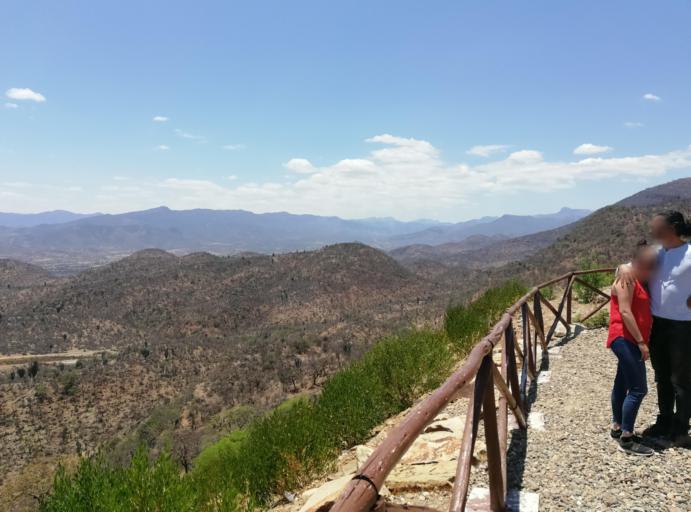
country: BO
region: Cochabamba
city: Aiquile
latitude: -18.1314
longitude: -64.8883
